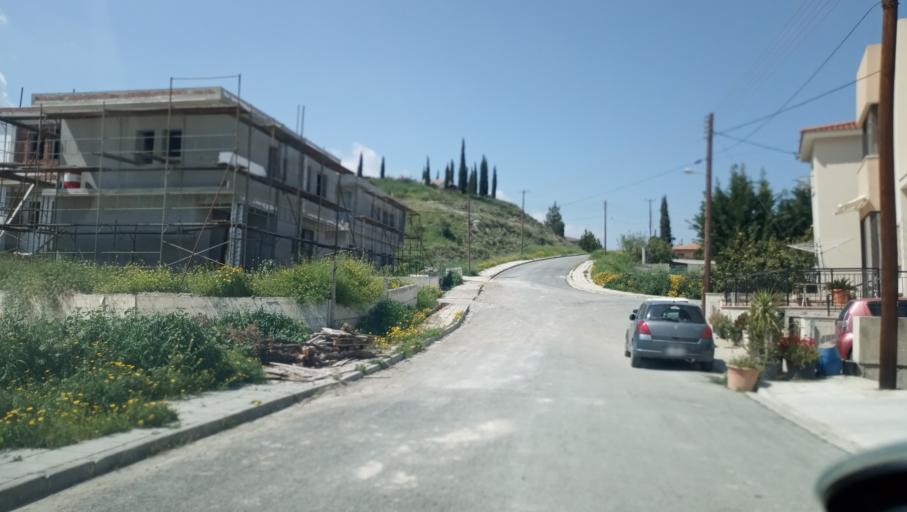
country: CY
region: Lefkosia
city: Alampra
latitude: 35.0102
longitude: 33.4025
